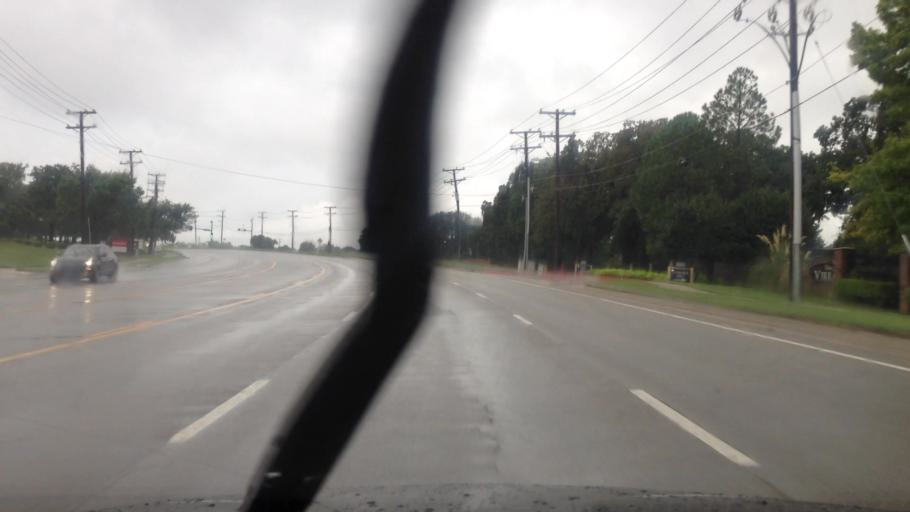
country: US
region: Texas
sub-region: Tarrant County
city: Colleyville
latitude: 32.8942
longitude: -97.2023
